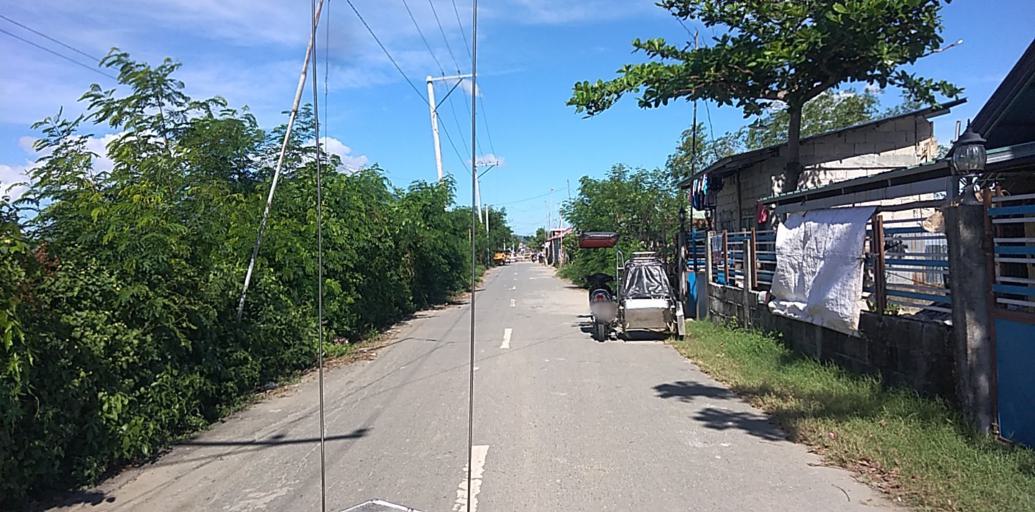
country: PH
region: Central Luzon
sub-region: Province of Pampanga
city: Candating
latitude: 15.1314
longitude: 120.8078
